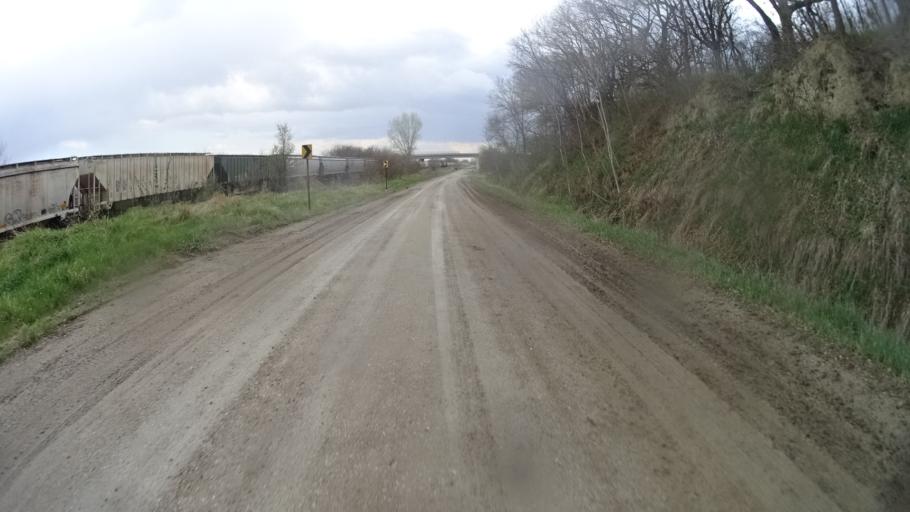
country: US
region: Nebraska
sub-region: Sarpy County
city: Offutt Air Force Base
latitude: 41.0843
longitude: -95.9168
